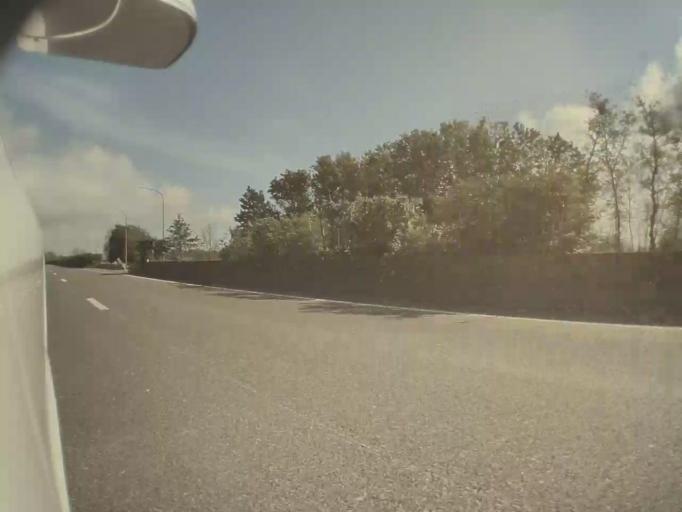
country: BE
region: Wallonia
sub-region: Province de Namur
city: Somme-Leuze
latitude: 50.2947
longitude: 5.3493
